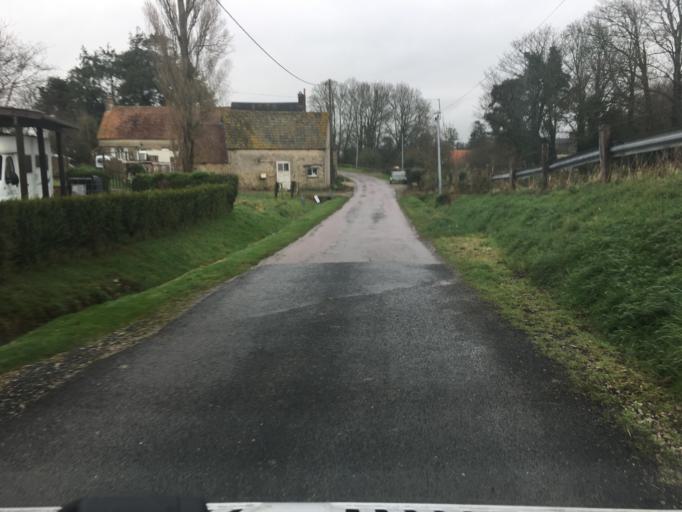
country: FR
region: Lower Normandy
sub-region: Departement de la Manche
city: Sainte-Mere-Eglise
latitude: 49.4263
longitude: -1.2644
